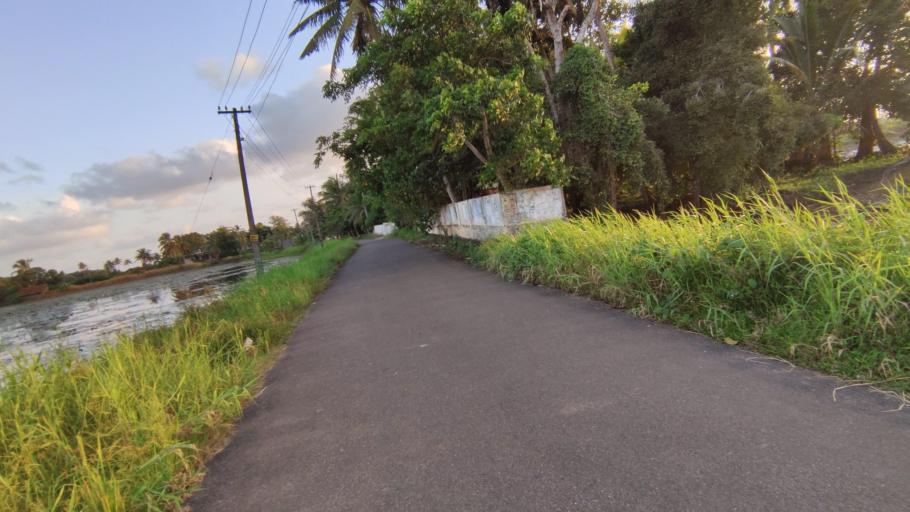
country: IN
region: Kerala
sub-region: Kottayam
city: Kottayam
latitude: 9.5905
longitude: 76.4485
